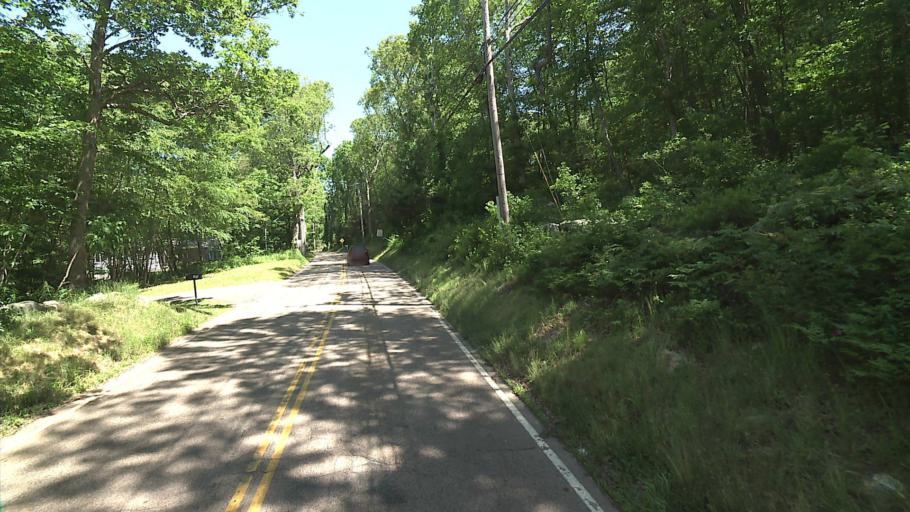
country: US
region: Connecticut
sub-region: New London County
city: Pawcatuck
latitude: 41.4377
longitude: -71.8476
